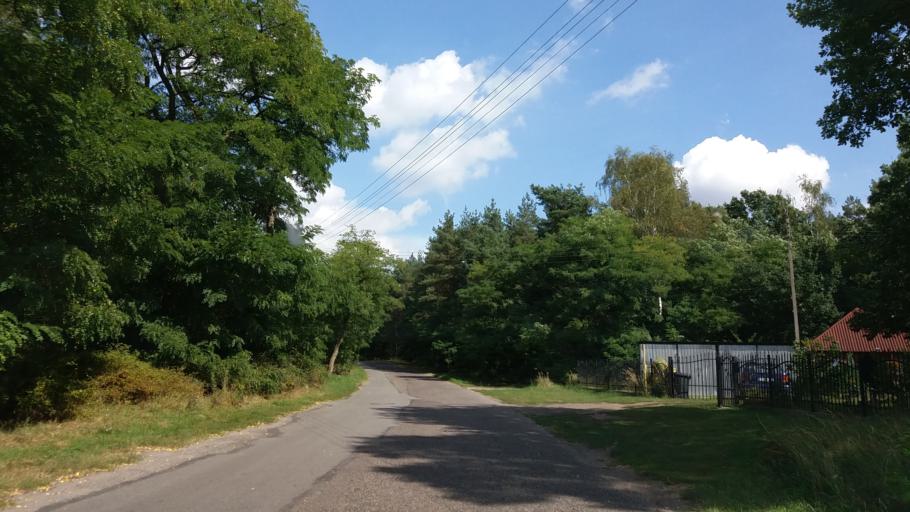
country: PL
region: West Pomeranian Voivodeship
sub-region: Powiat stargardzki
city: Kobylanka
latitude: 53.3666
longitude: 14.8781
